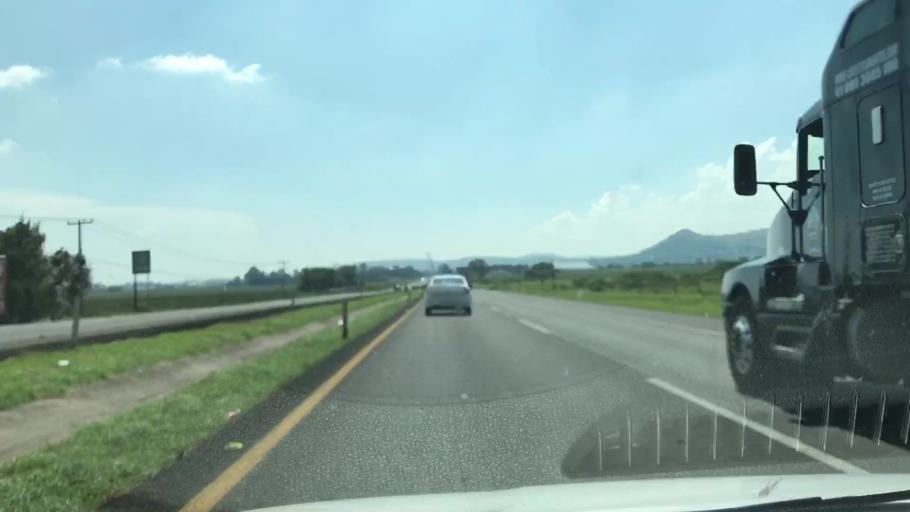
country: MX
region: Guanajuato
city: Penjamo
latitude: 20.4383
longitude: -101.6810
